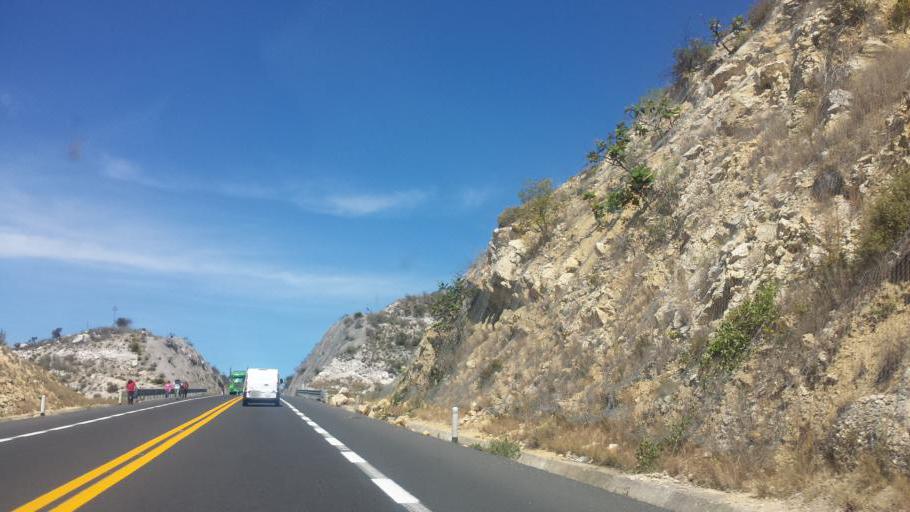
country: MX
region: Puebla
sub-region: San Jose Miahuatlan
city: San Pedro Tetitlan
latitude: 17.9963
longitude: -97.3547
